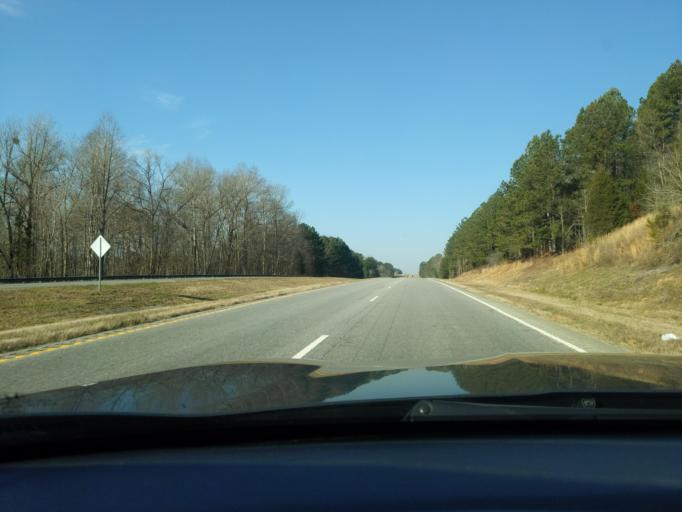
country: US
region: South Carolina
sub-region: Abbeville County
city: Abbeville
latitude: 34.1835
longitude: -82.3058
